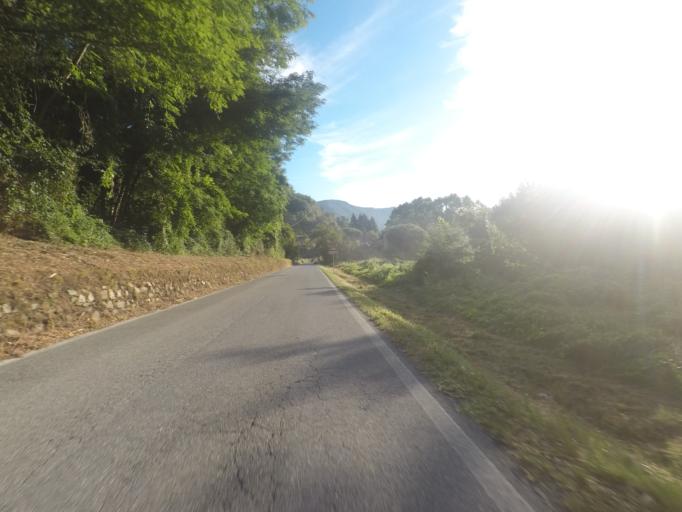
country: IT
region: Tuscany
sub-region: Provincia di Lucca
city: Valdottavo
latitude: 43.9597
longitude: 10.4559
